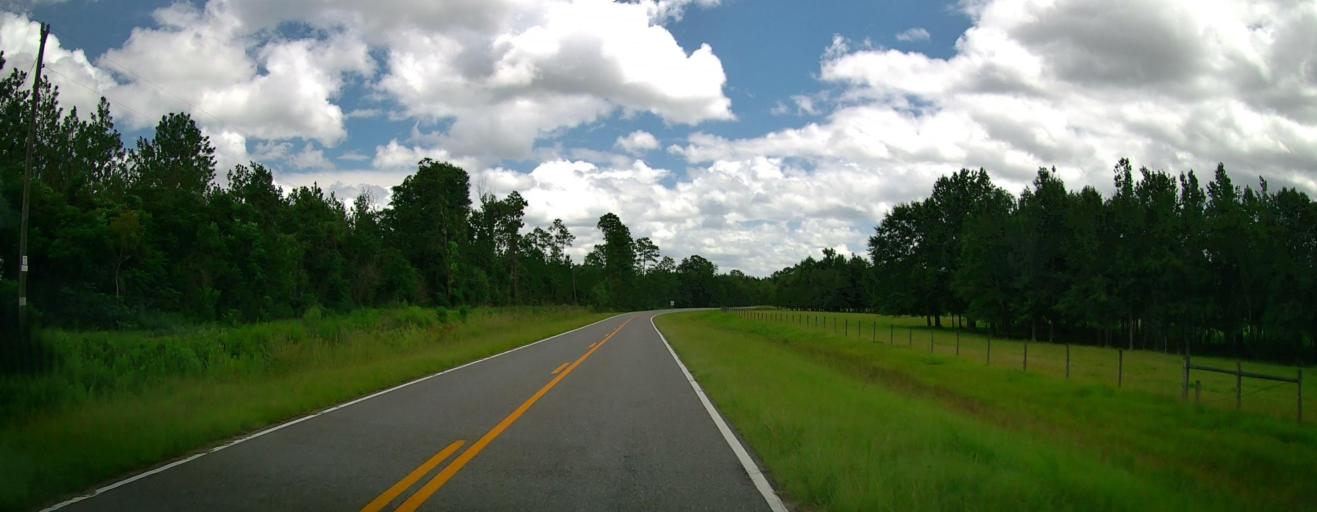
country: US
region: Georgia
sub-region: Turner County
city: Ashburn
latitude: 31.6961
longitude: -83.4806
